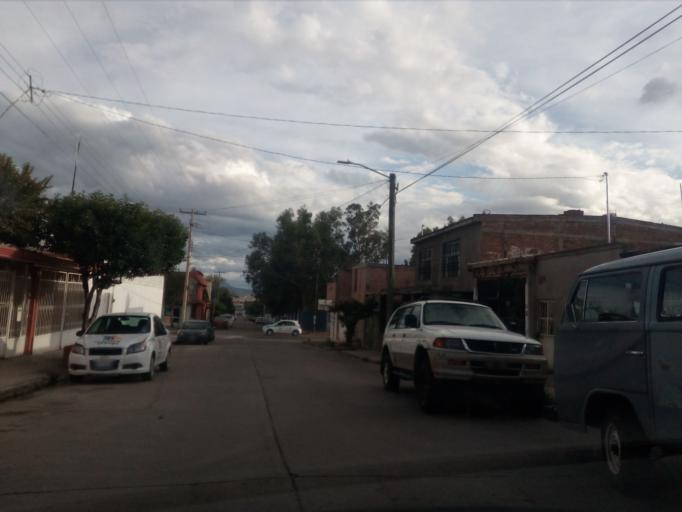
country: MX
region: Durango
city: Victoria de Durango
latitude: 24.0419
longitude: -104.6656
